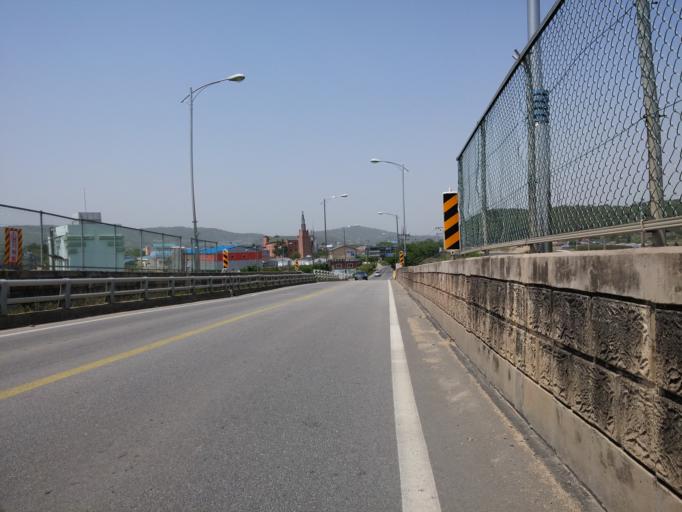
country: KR
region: Chungcheongnam-do
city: Nonsan
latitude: 36.2138
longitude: 127.2051
